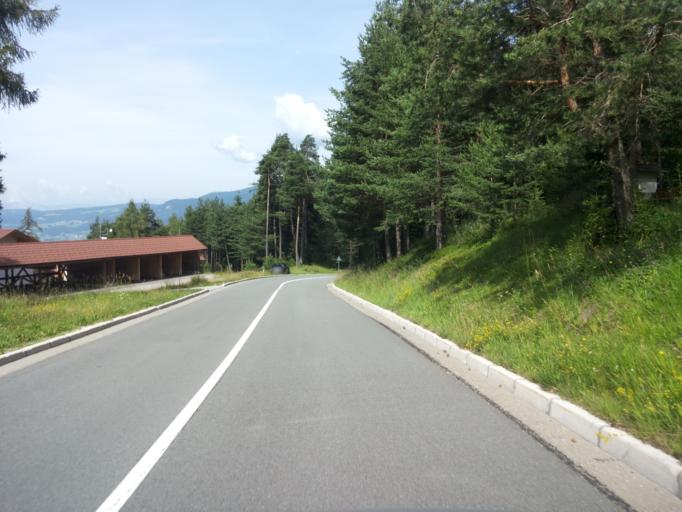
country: IT
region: Trentino-Alto Adige
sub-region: Bolzano
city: Castelrotto
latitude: 46.5805
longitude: 11.6042
